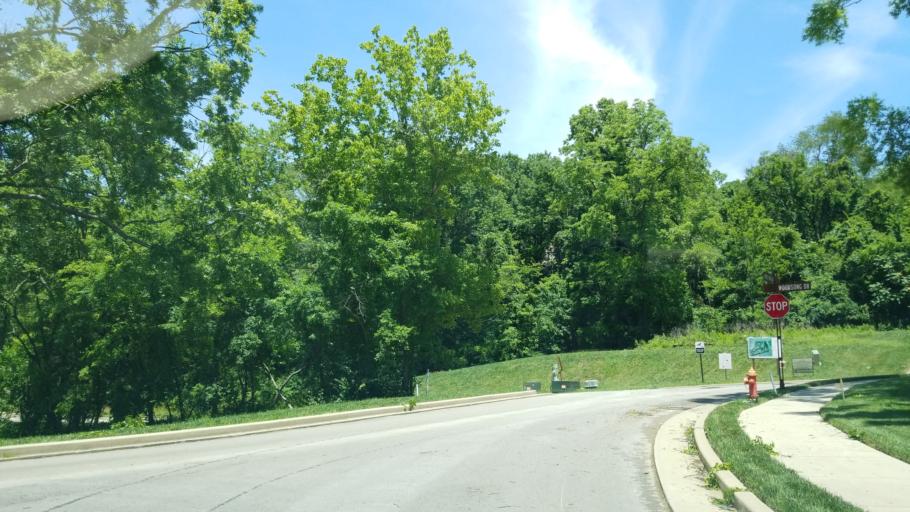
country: US
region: Tennessee
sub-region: Williamson County
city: Brentwood
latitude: 36.0500
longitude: -86.8134
